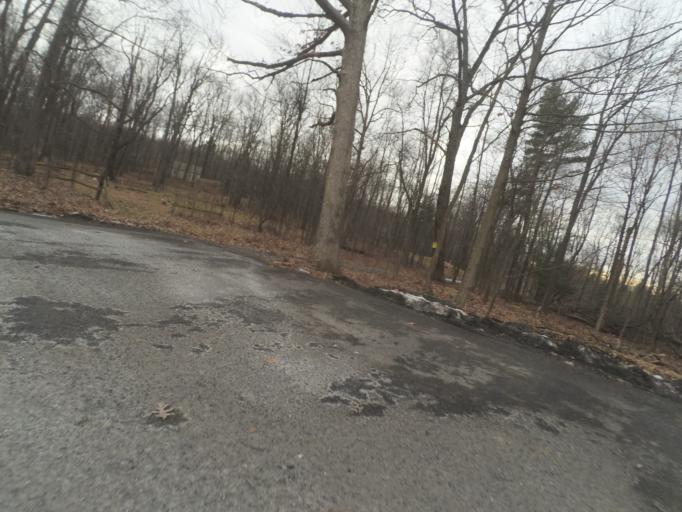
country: US
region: Pennsylvania
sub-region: Centre County
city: Stormstown
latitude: 40.8645
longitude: -77.9988
